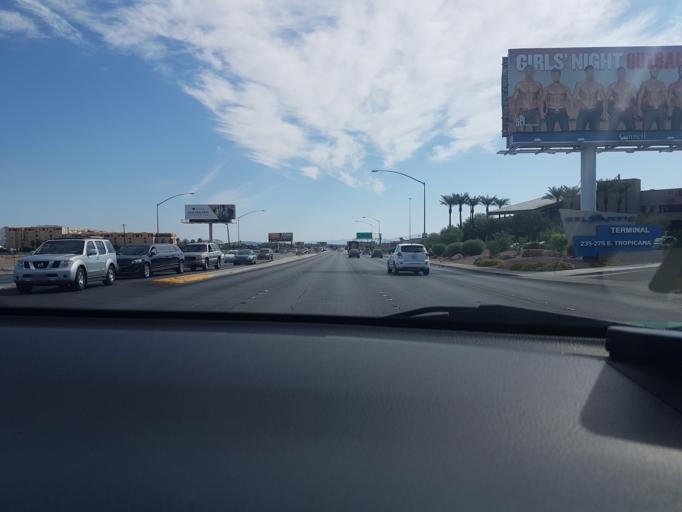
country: US
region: Nevada
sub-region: Clark County
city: Paradise
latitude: 36.1008
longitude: -115.1617
